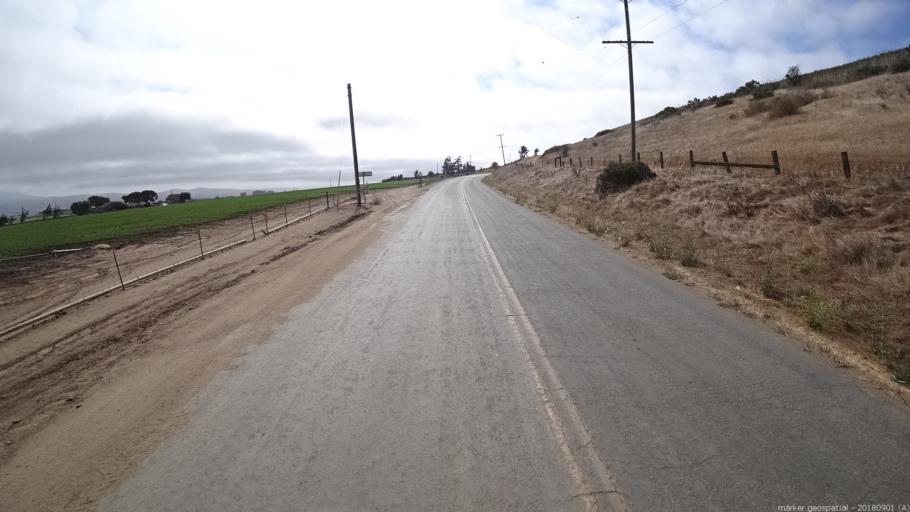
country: US
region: California
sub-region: Monterey County
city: Soledad
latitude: 36.3777
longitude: -121.3396
